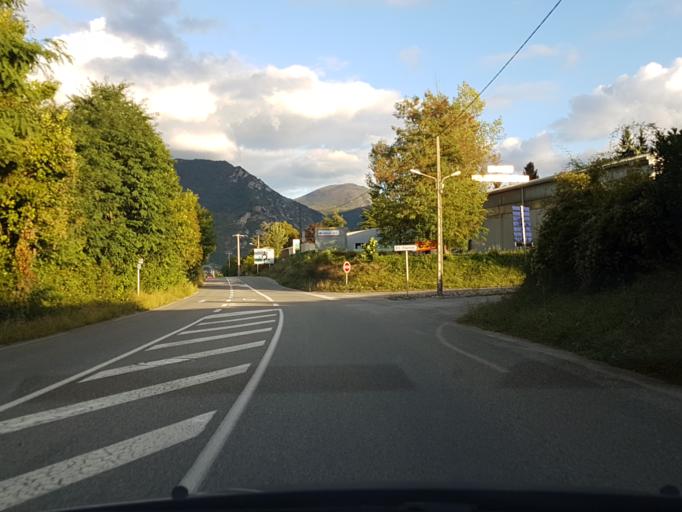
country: FR
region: Midi-Pyrenees
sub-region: Departement de l'Ariege
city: Tarascon-sur-Ariege
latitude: 42.8546
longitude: 1.5861
